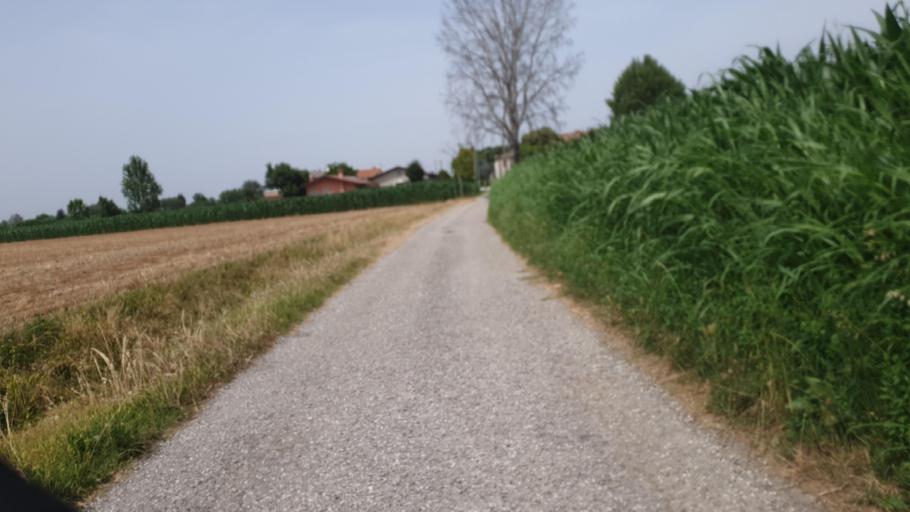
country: IT
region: Veneto
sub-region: Provincia di Padova
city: Polverara
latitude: 45.2933
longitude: 11.9512
